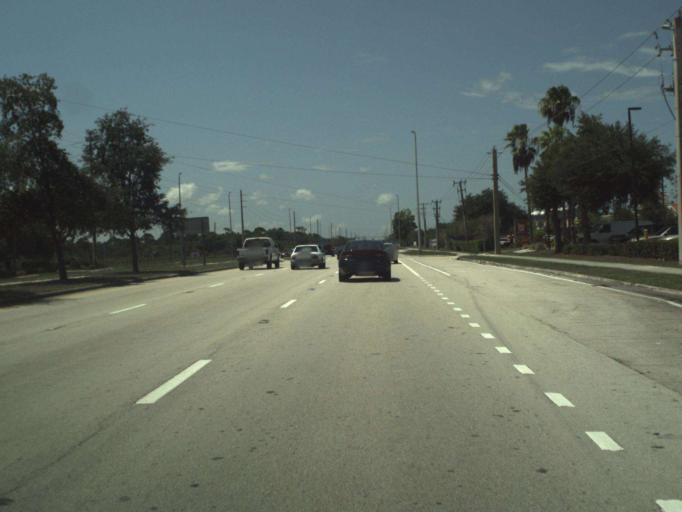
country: US
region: Florida
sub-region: Saint Lucie County
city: River Park
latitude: 27.3006
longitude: -80.3054
